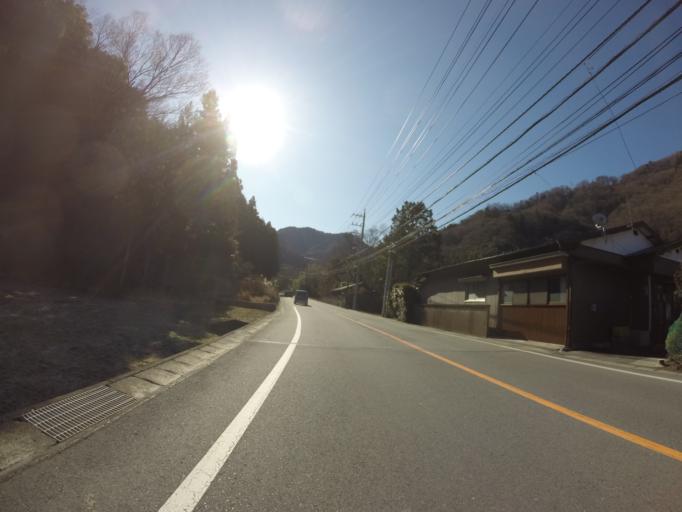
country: JP
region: Yamanashi
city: Ryuo
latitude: 35.4318
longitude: 138.4091
